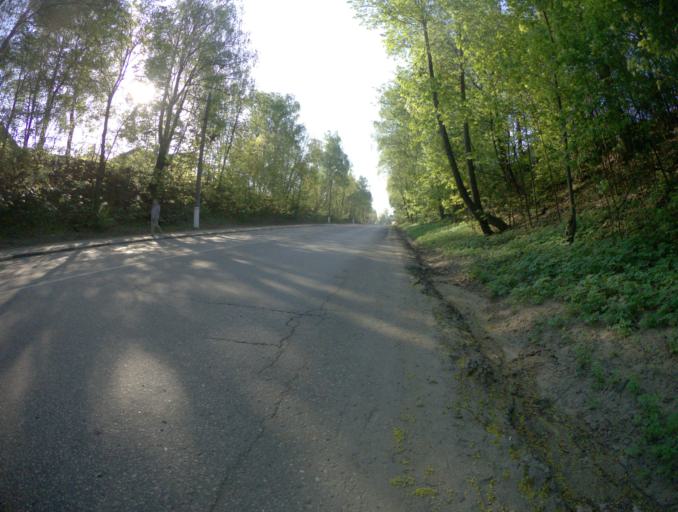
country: RU
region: Vladimir
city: Vyazniki
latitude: 56.2406
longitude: 42.1699
